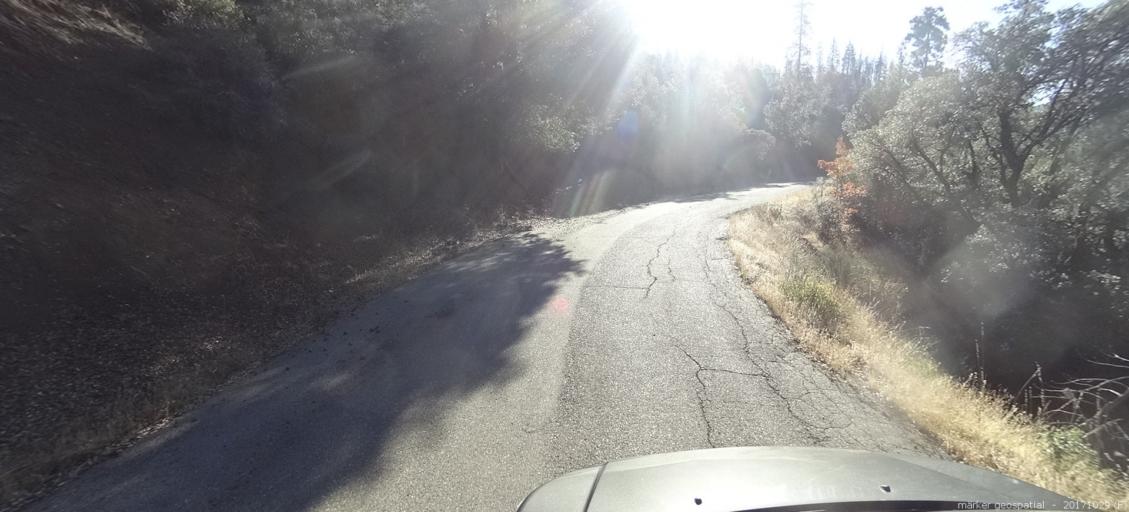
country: US
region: California
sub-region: Trinity County
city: Hayfork
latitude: 40.3793
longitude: -122.9785
